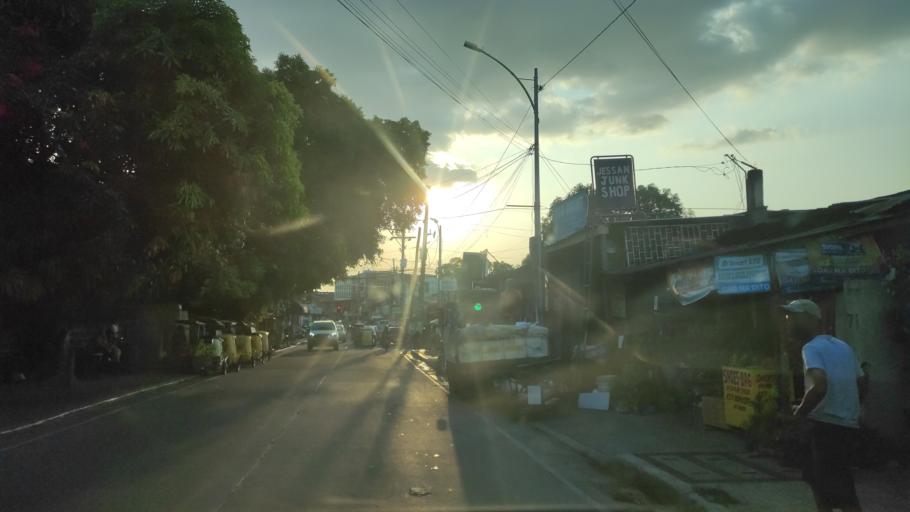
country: PH
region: Calabarzon
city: Bagong Pagasa
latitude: 14.6684
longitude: 121.0213
